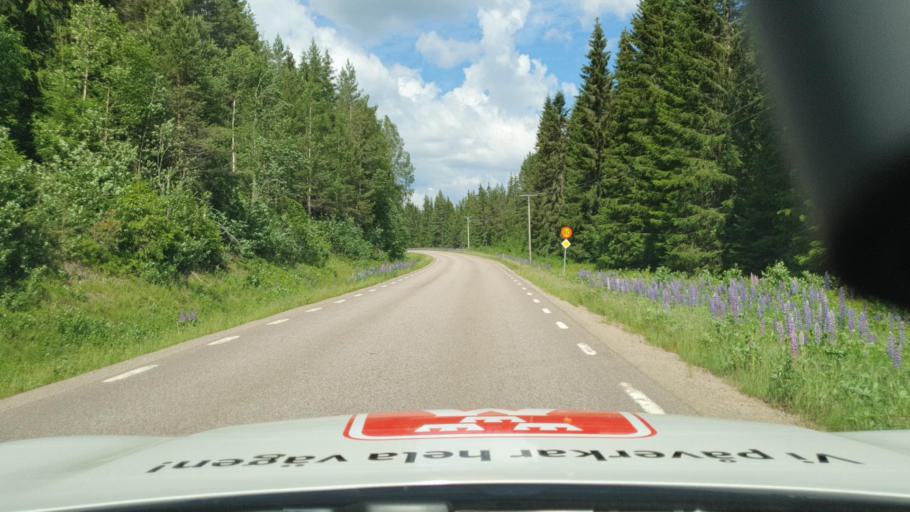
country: SE
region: Vaermland
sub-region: Torsby Kommun
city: Torsby
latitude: 60.4719
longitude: 12.8842
